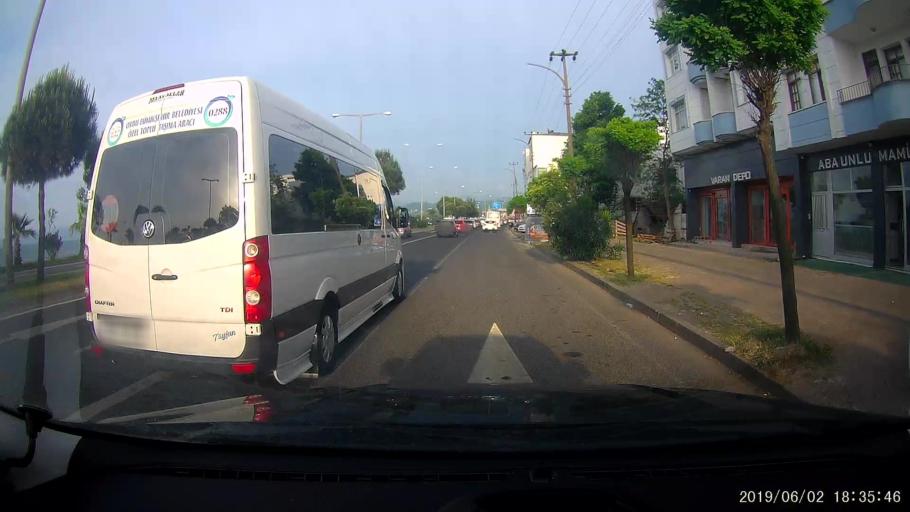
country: TR
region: Ordu
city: Fatsa
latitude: 41.0256
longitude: 37.5200
